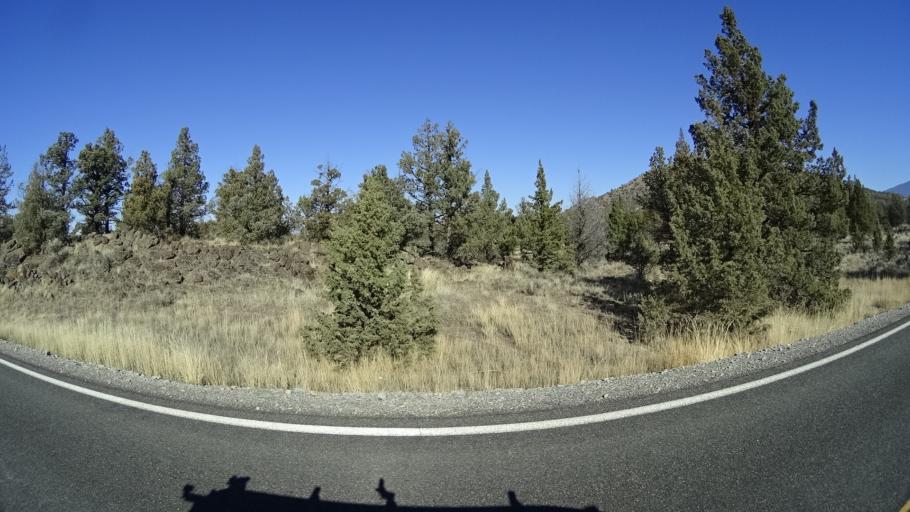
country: US
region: California
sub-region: Siskiyou County
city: Montague
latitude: 41.6596
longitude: -122.3966
